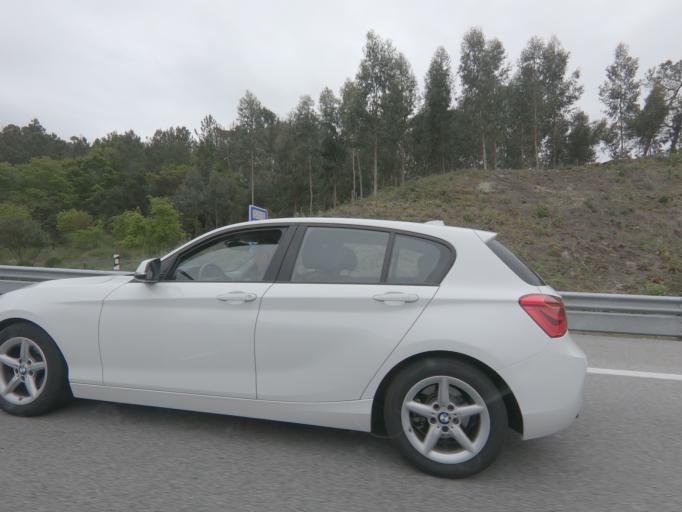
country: PT
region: Viseu
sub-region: Viseu
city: Viseu
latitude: 40.6242
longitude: -7.9513
